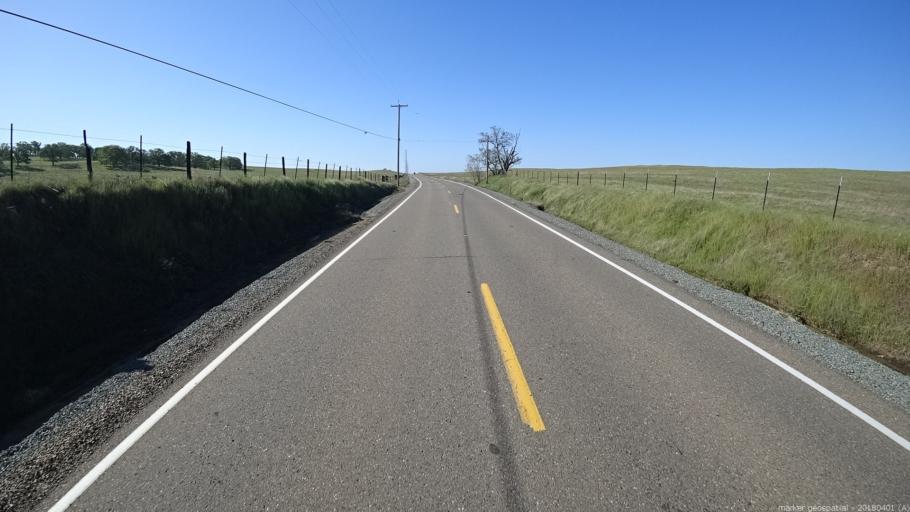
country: US
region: California
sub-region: Sacramento County
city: Rancho Murieta
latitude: 38.4570
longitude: -121.0446
